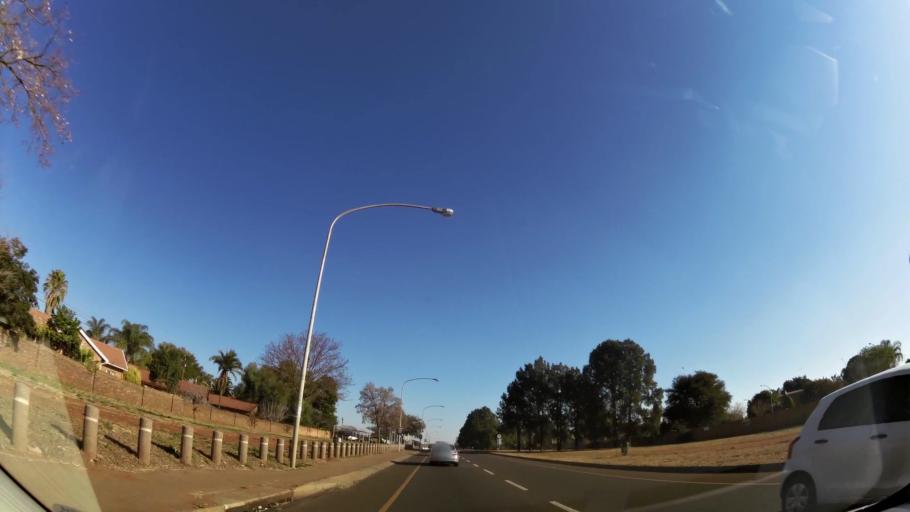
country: ZA
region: Gauteng
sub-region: City of Tshwane Metropolitan Municipality
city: Centurion
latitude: -25.8644
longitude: 28.1577
